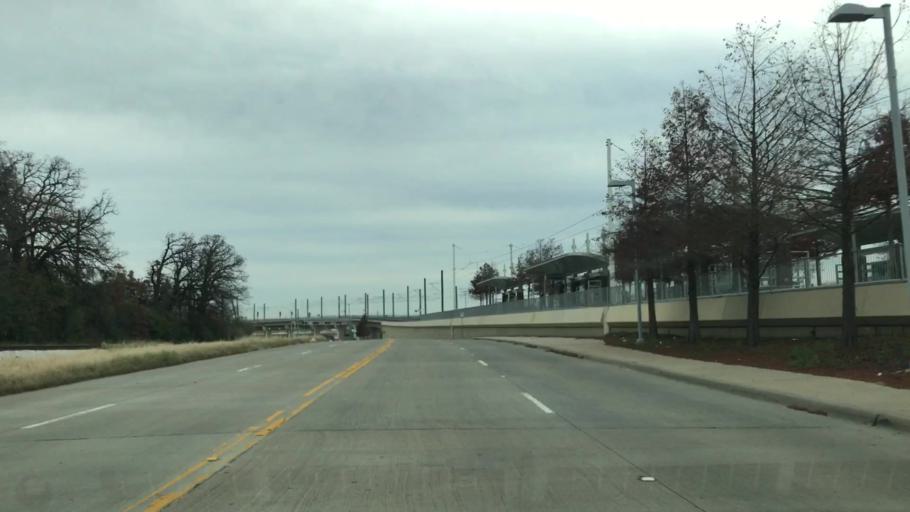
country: US
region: Texas
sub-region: Dallas County
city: Farmers Branch
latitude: 32.8544
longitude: -96.8772
